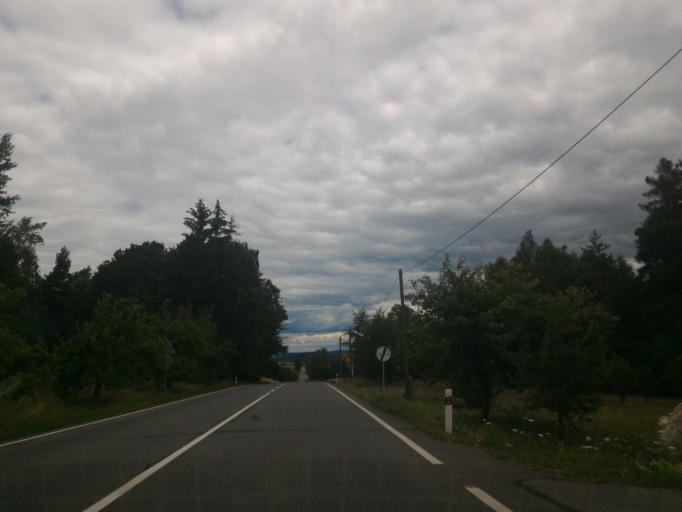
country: CZ
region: Vysocina
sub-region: Okres Pelhrimov
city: Zeliv
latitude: 49.4861
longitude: 15.1791
